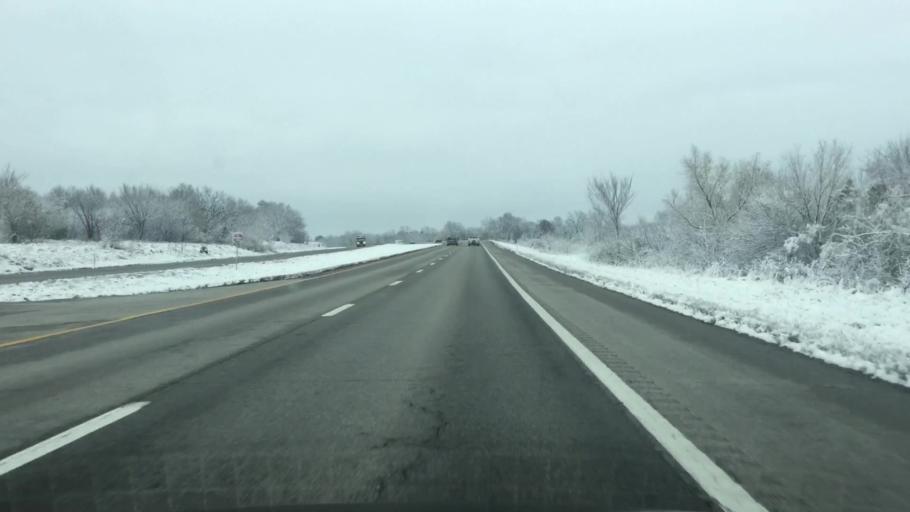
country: US
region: Missouri
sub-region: Cass County
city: Garden City
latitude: 38.5219
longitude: -94.1430
